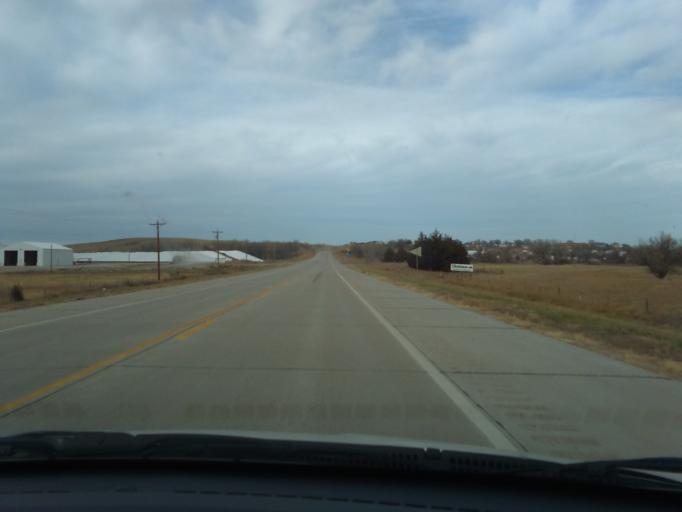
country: US
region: Nebraska
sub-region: Dundy County
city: Benkelman
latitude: 40.0363
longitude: -101.5432
